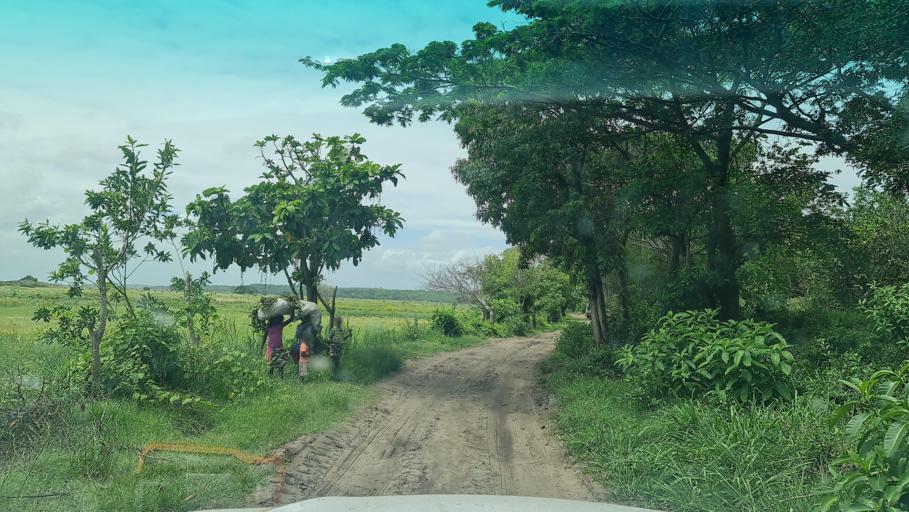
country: MZ
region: Maputo
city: Manhica
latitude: -25.5225
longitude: 32.8615
